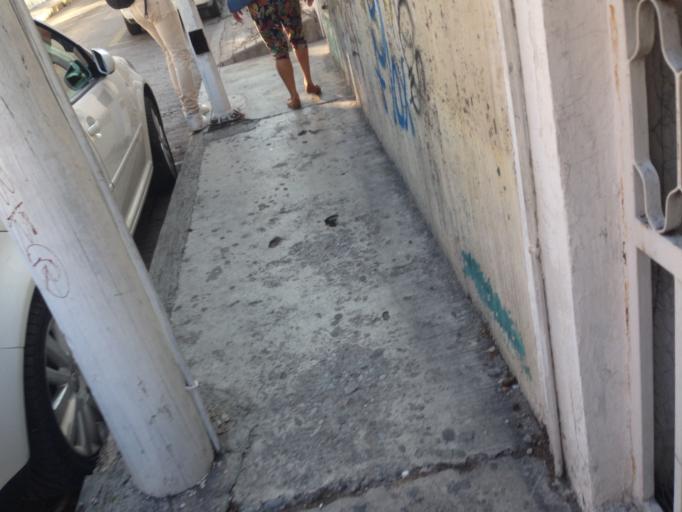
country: MX
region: Guerrero
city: Chilpancingo de los Bravos
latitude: 17.5539
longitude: -99.4987
